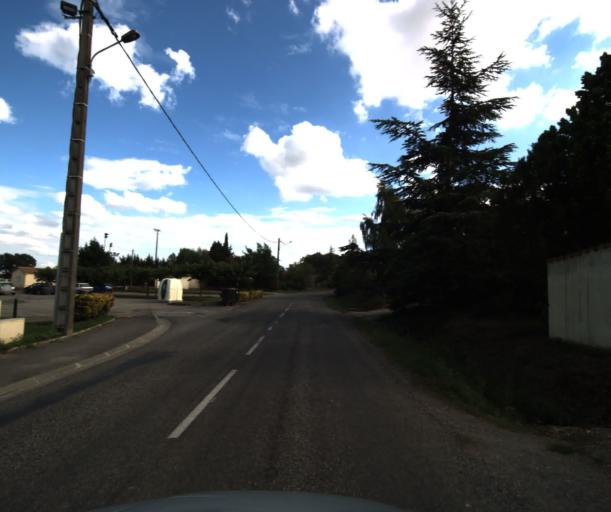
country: FR
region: Midi-Pyrenees
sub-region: Departement de la Haute-Garonne
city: Saubens
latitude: 43.4755
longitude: 1.3524
